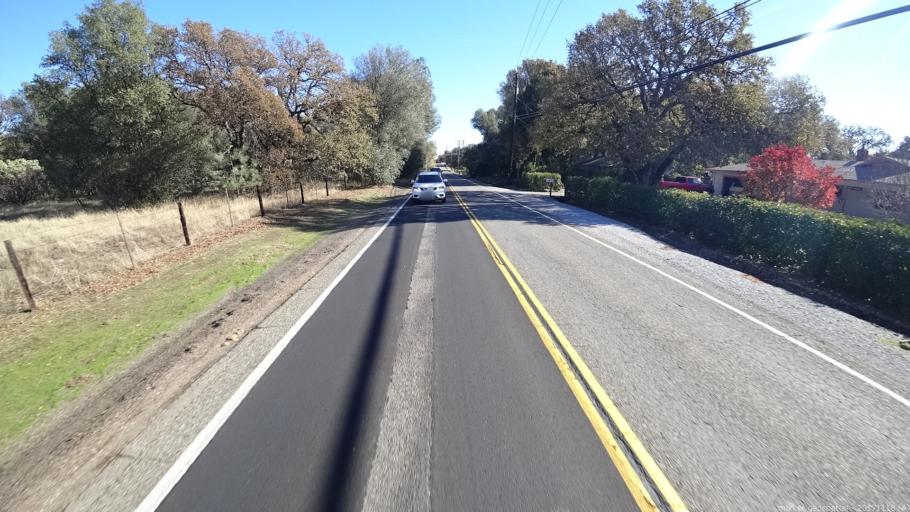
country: US
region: California
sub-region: Shasta County
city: Cottonwood
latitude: 40.3895
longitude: -122.3452
